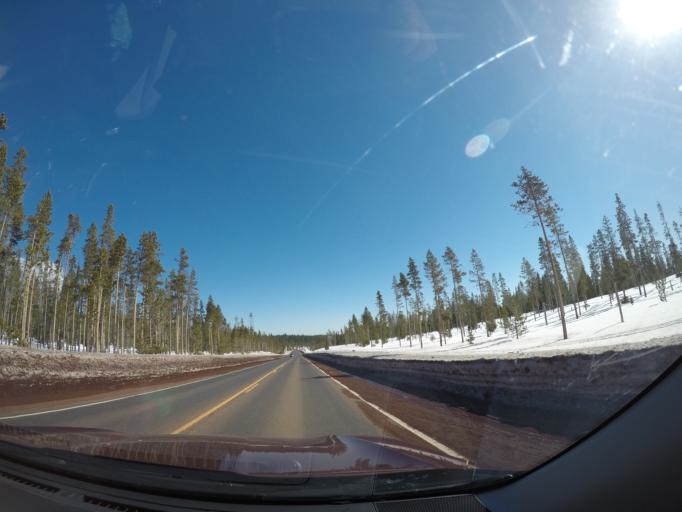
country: US
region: Oregon
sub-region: Deschutes County
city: Sunriver
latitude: 43.9863
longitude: -121.5747
